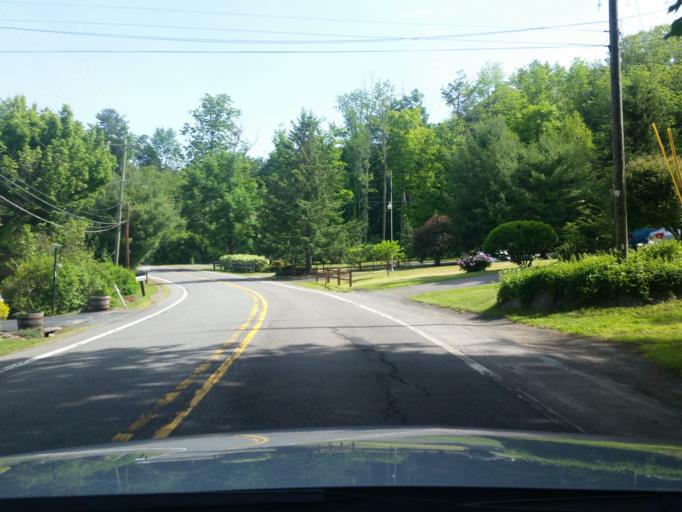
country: US
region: Pennsylvania
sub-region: Luzerne County
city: Harveys Lake
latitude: 41.3783
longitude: -76.0256
